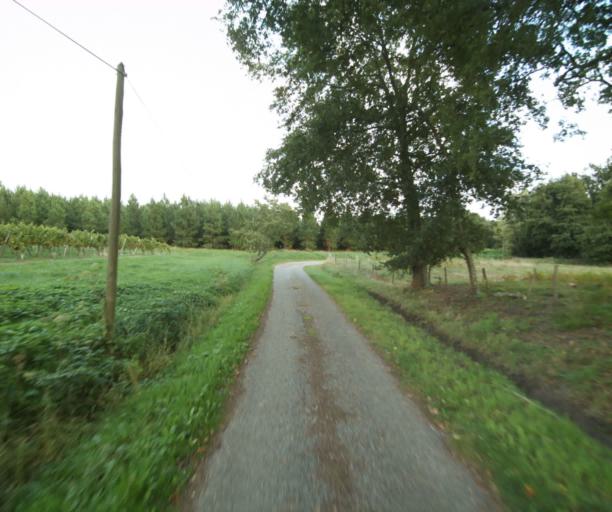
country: FR
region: Aquitaine
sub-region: Departement des Landes
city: Gabarret
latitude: 43.9727
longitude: 0.0816
